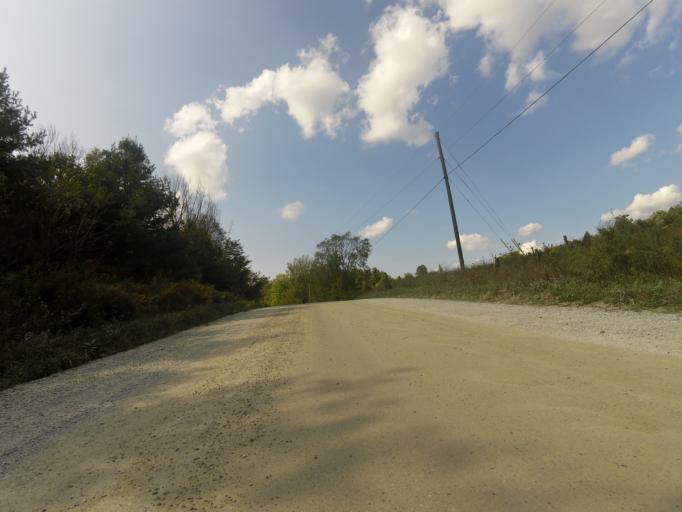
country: CA
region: Ontario
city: Renfrew
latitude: 45.1475
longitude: -76.6741
